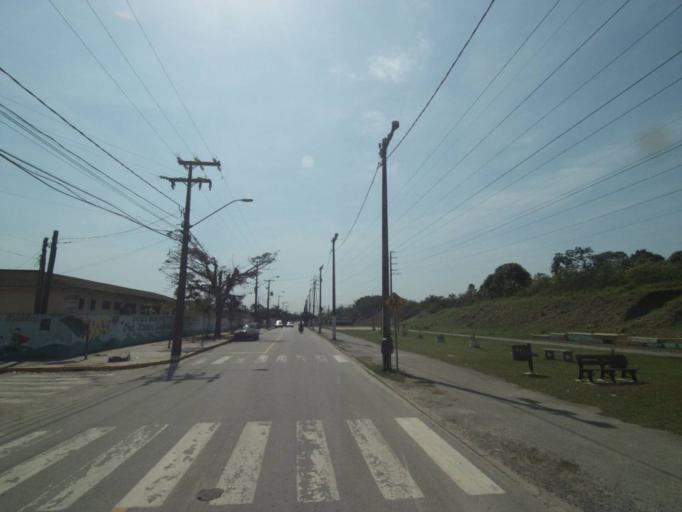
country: BR
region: Parana
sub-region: Paranagua
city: Paranagua
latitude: -25.5428
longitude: -48.5471
